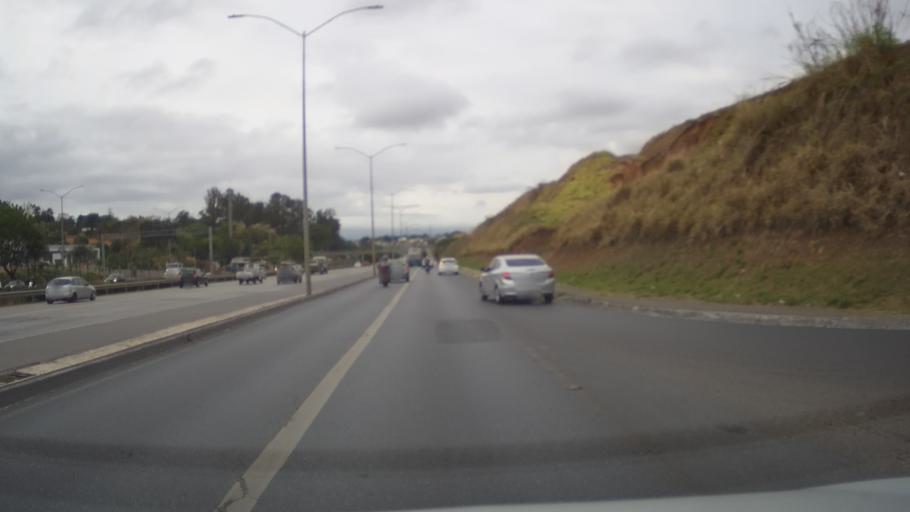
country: BR
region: Minas Gerais
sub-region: Santa Luzia
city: Santa Luzia
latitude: -19.8017
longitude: -43.9502
